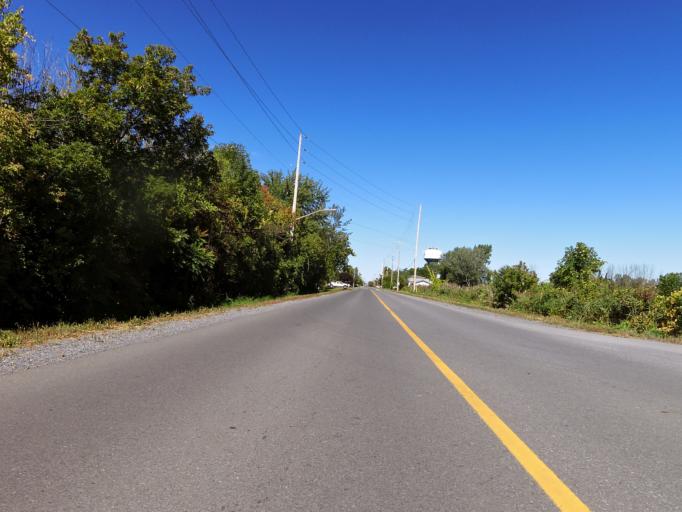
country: CA
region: Ontario
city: Casselman
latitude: 45.2668
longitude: -75.2712
